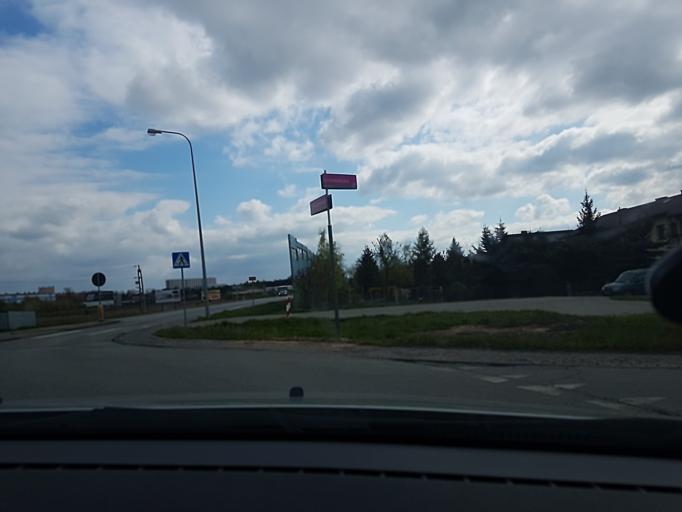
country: PL
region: Lodz Voivodeship
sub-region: Powiat kutnowski
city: Kutno
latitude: 52.2274
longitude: 19.3866
